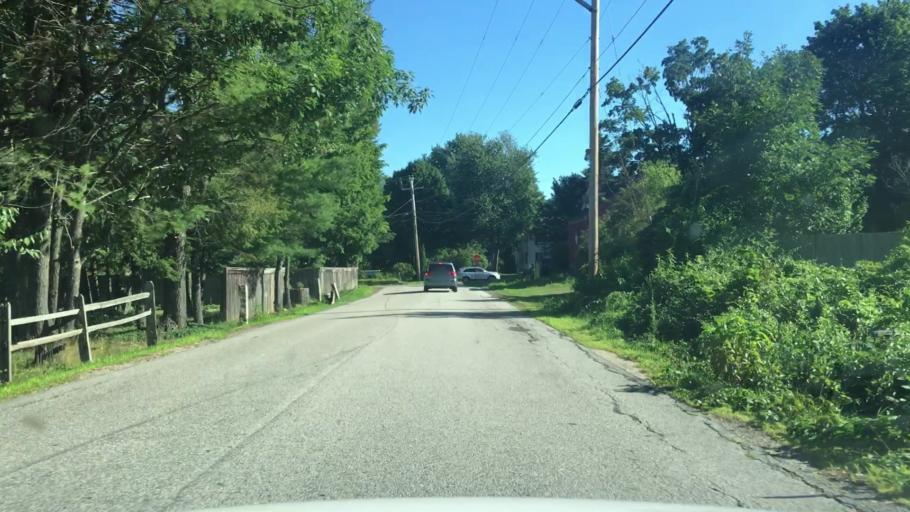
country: US
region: New Hampshire
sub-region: Rockingham County
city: Brentwood
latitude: 42.9931
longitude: -71.0147
